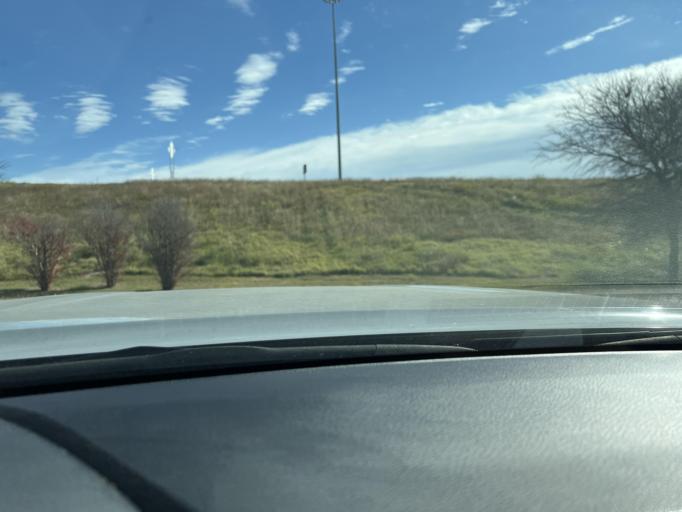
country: US
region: Texas
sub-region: Eastland County
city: Eastland
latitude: 32.4007
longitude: -98.7908
